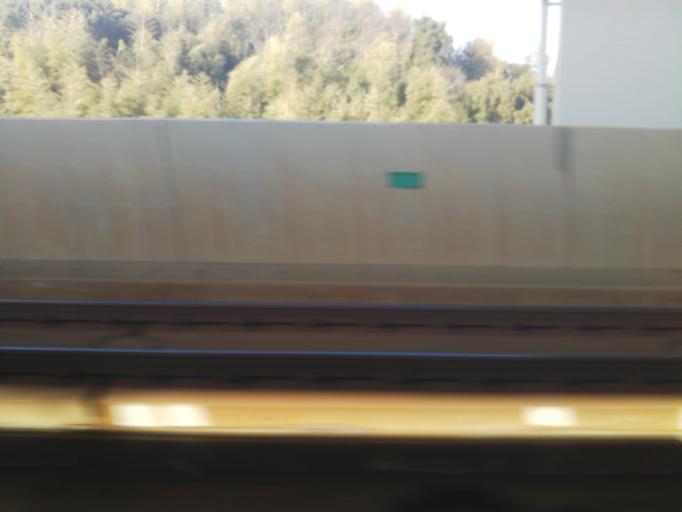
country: JP
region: Kagawa
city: Sakaidecho
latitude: 34.4166
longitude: 133.8049
